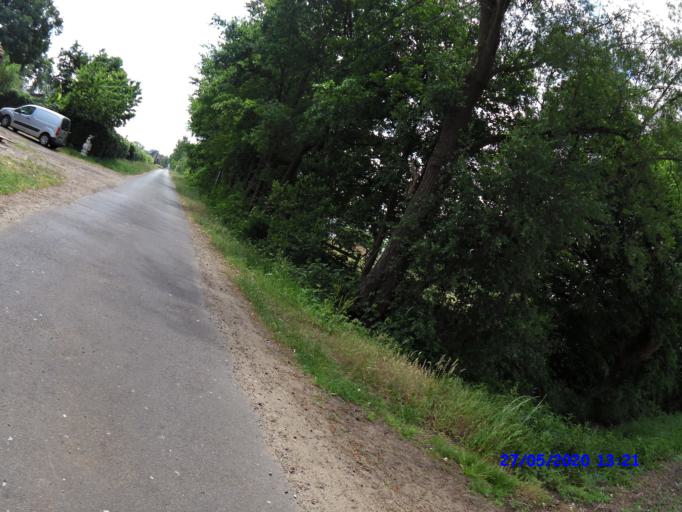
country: BE
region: Flanders
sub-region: Provincie Antwerpen
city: Geel
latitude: 51.2027
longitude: 5.0003
